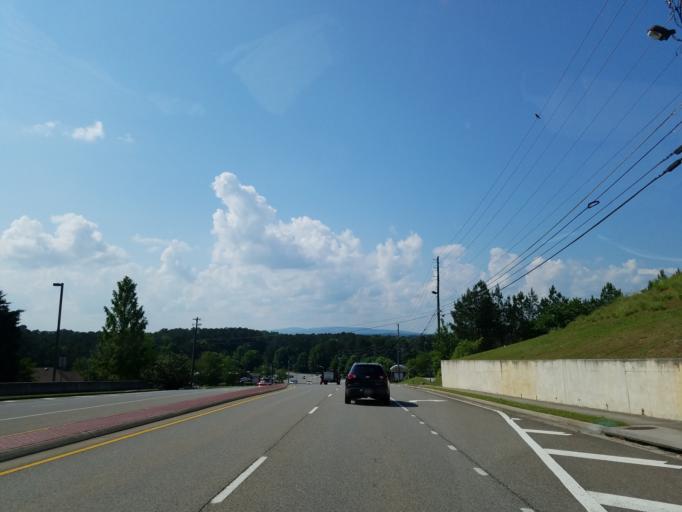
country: US
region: Georgia
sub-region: Cherokee County
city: Holly Springs
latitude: 34.1767
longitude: -84.5491
